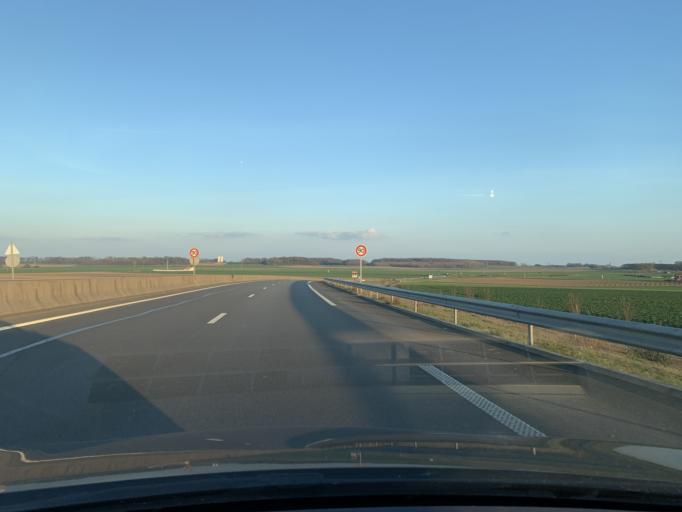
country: FR
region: Nord-Pas-de-Calais
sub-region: Departement du Nord
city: Cantin
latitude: 50.3216
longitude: 3.1242
